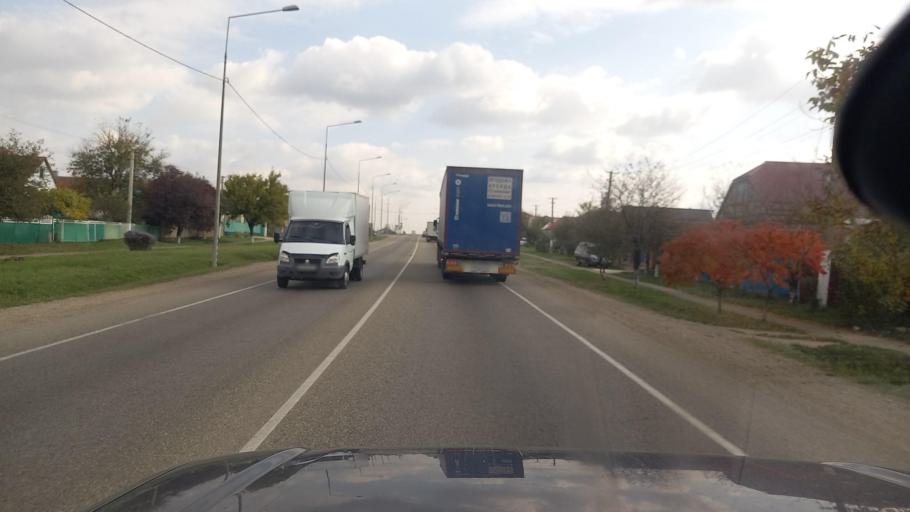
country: RU
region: Krasnodarskiy
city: Kholmskiy
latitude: 44.8482
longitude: 38.4081
